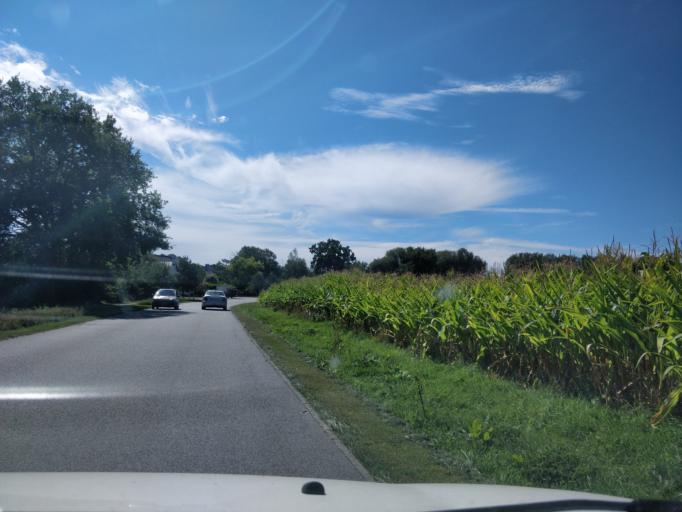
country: FR
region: Brittany
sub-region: Departement du Morbihan
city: Saint-Philibert
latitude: 47.5941
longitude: -2.9989
